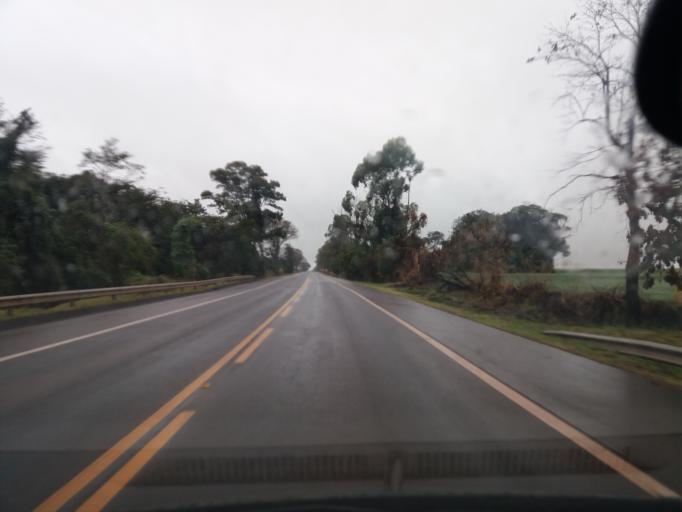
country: BR
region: Parana
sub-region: Campo Mourao
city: Campo Mourao
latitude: -24.3183
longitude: -52.6255
